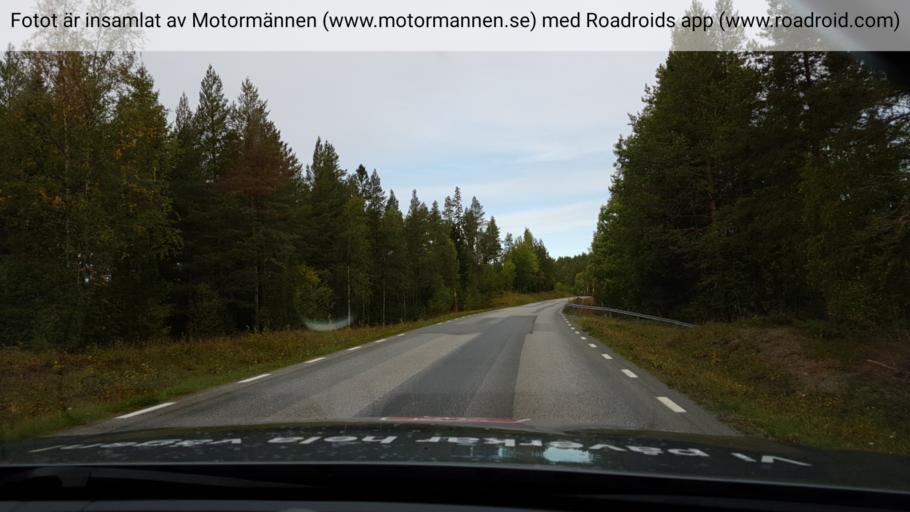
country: SE
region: Jaemtland
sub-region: Krokoms Kommun
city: Krokom
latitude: 63.2832
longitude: 14.2704
